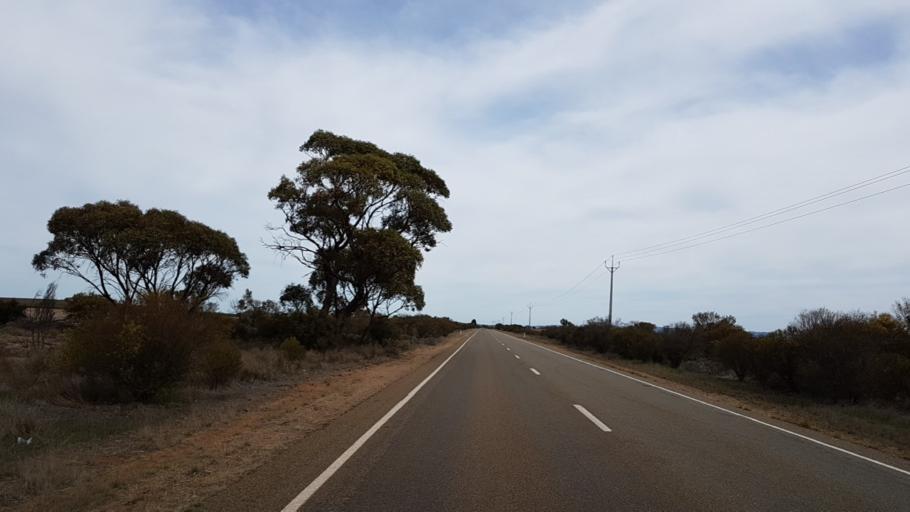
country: AU
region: South Australia
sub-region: Peterborough
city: Peterborough
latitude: -32.9868
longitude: 138.8003
